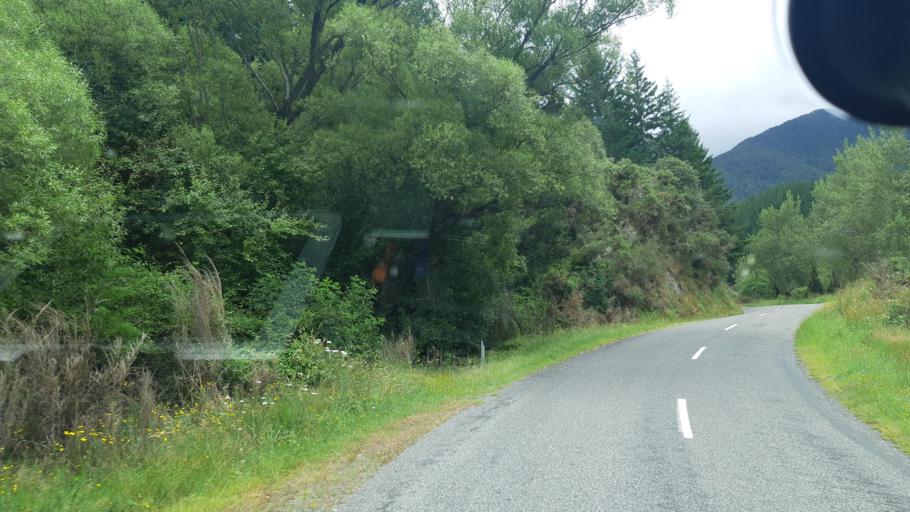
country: NZ
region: Marlborough
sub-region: Marlborough District
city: Blenheim
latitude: -41.4521
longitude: 173.7211
